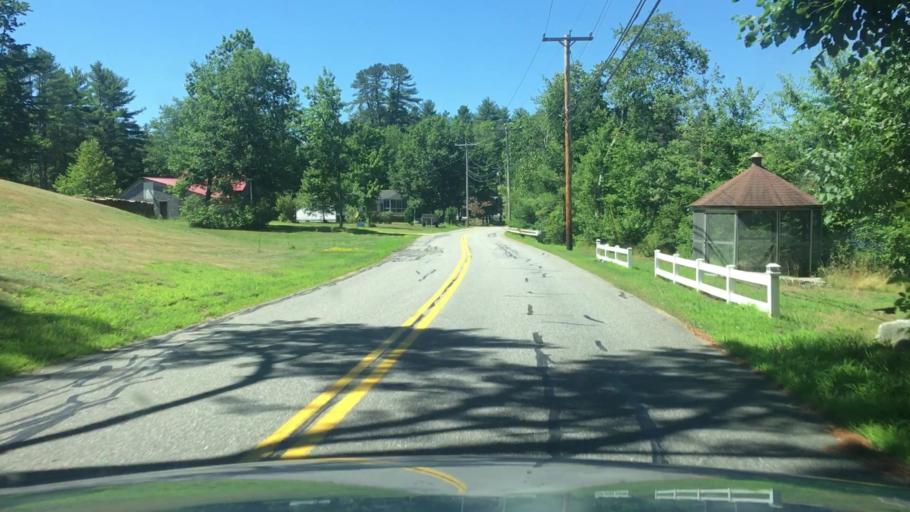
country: US
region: New Hampshire
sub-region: Merrimack County
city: Boscawen
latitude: 43.2638
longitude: -71.6141
